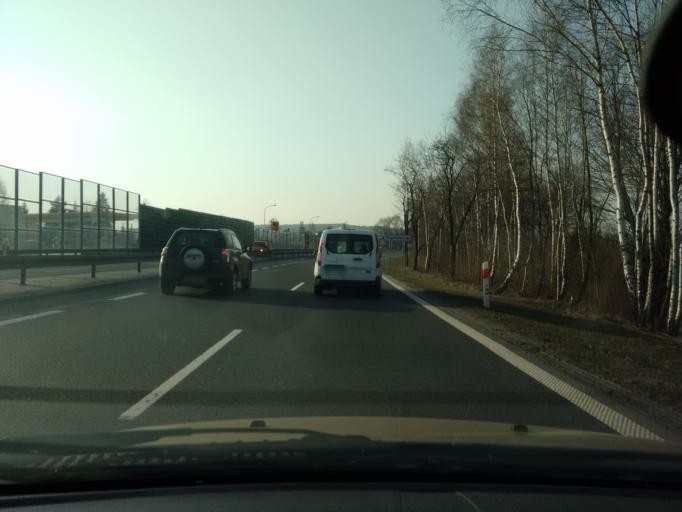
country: PL
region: Silesian Voivodeship
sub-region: Powiat cieszynski
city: Skoczow
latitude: 49.7913
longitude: 18.7992
